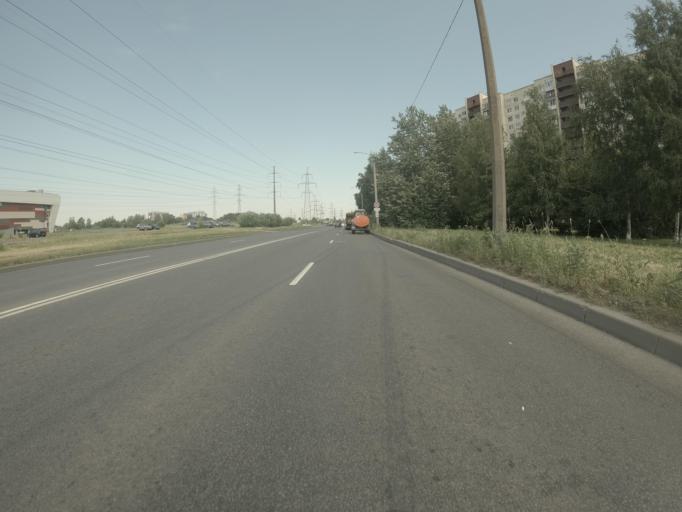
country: RU
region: St.-Petersburg
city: Krasnogvargeisky
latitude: 59.9472
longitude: 30.4611
